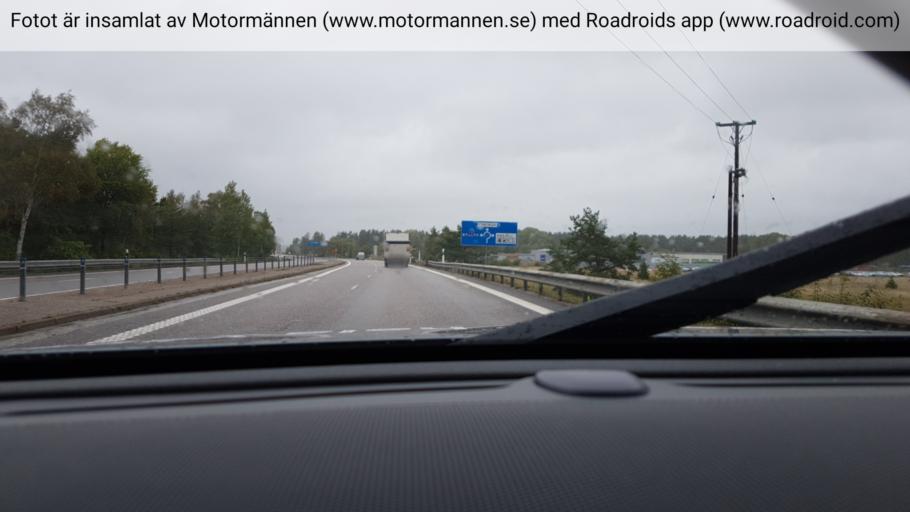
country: SE
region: Vaestra Goetaland
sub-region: Vanersborgs Kommun
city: Vanersborg
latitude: 58.3525
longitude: 12.3153
